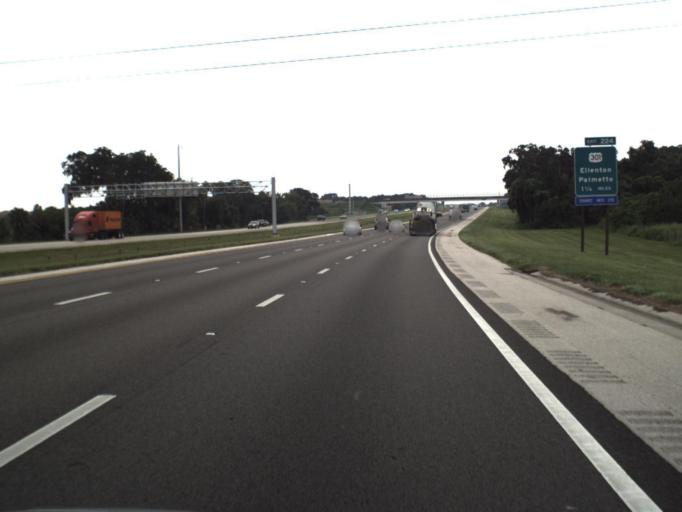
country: US
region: Florida
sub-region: Manatee County
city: Ellenton
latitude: 27.5525
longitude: -82.5112
